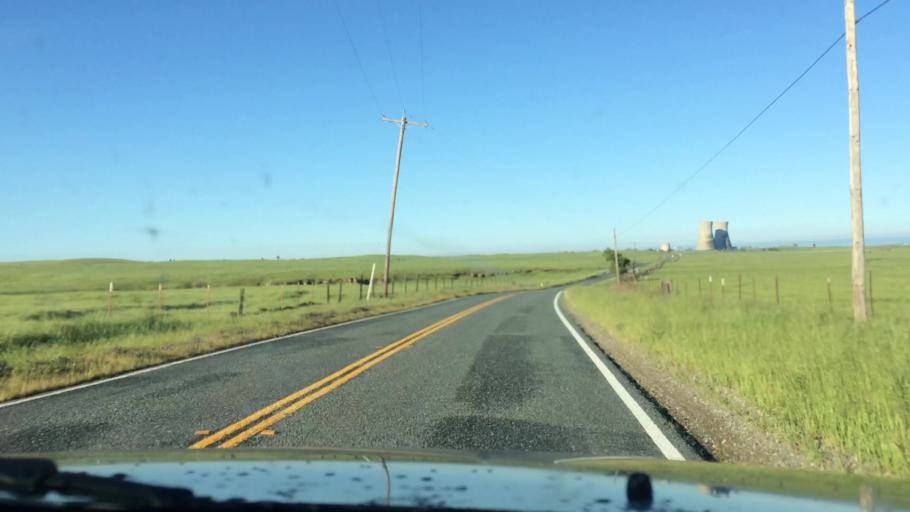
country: US
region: California
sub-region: Sacramento County
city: Clay
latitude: 38.3615
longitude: -121.0824
